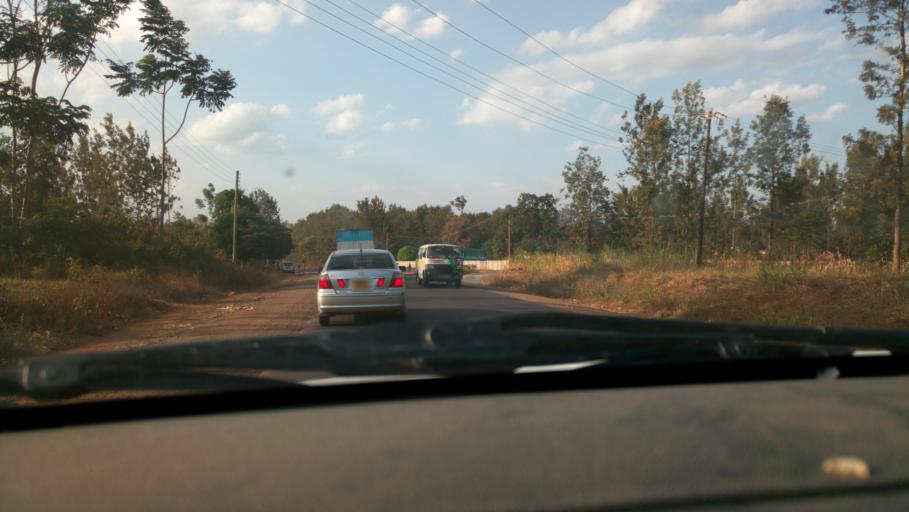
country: KE
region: Murang'a District
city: Maragua
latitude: -0.8102
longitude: 37.1407
